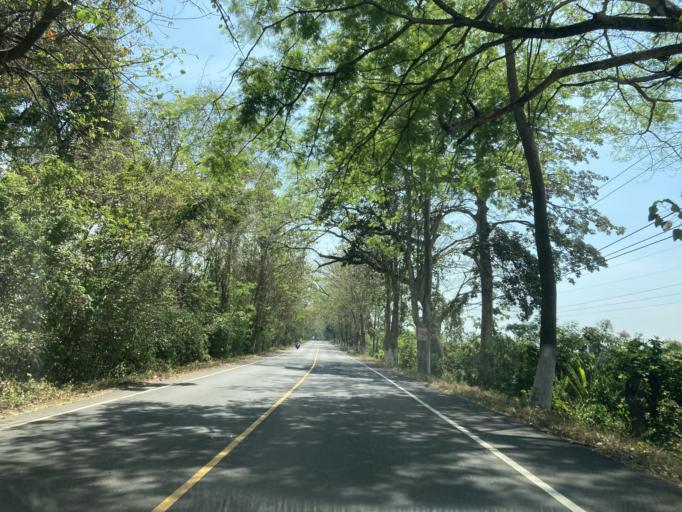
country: GT
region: Escuintla
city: Guanagazapa
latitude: 14.1828
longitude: -90.6909
